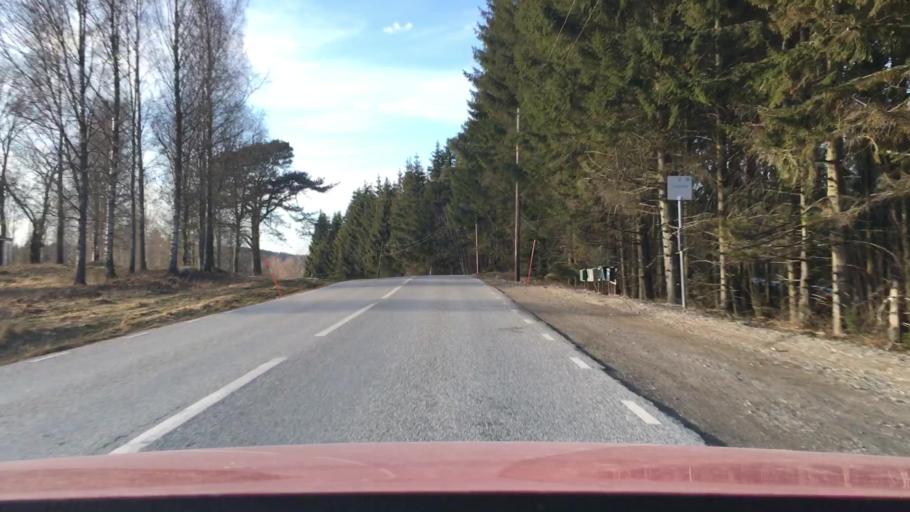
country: SE
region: Vaestra Goetaland
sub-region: Tanums Kommun
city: Tanumshede
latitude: 58.8106
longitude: 11.5498
